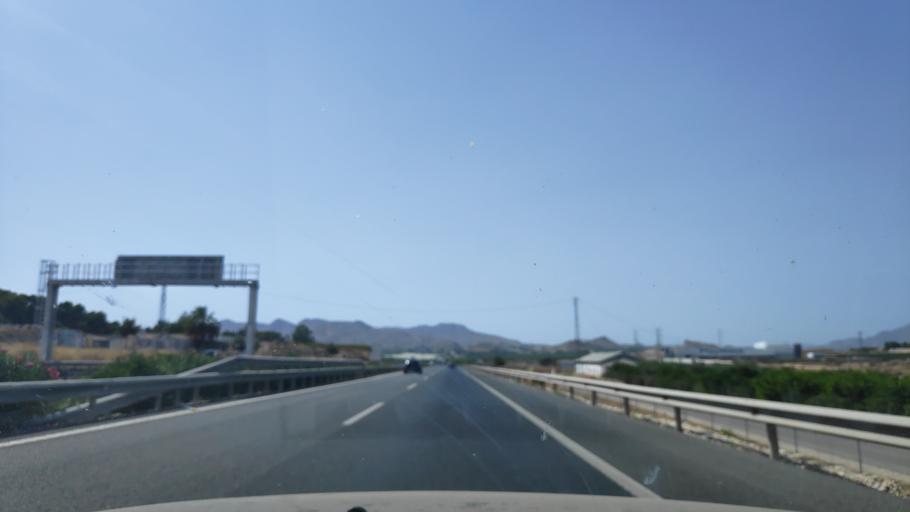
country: ES
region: Murcia
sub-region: Murcia
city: Archena
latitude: 38.1315
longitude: -1.2647
